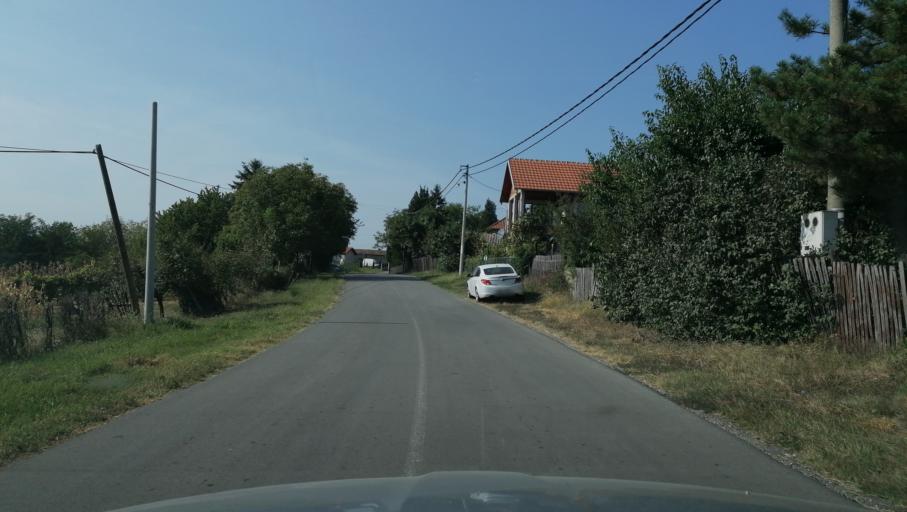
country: RS
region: Central Serbia
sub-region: Belgrade
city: Sopot
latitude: 44.6006
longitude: 20.6046
